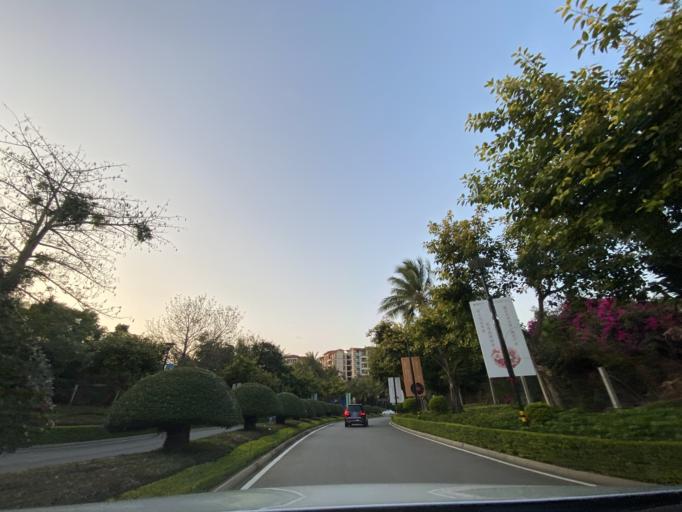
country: CN
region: Hainan
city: Yingzhou
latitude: 18.3959
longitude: 109.8560
